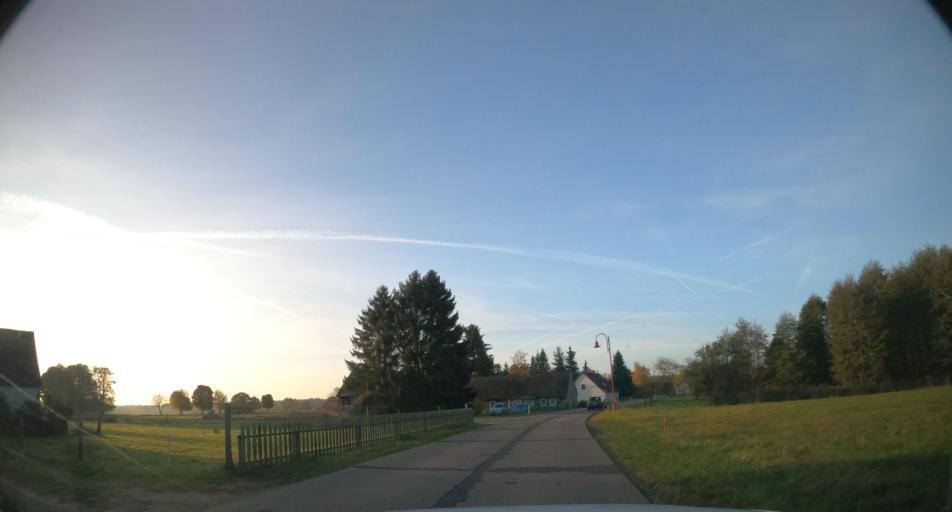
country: DE
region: Mecklenburg-Vorpommern
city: Ahlbeck
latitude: 53.6238
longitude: 14.2639
